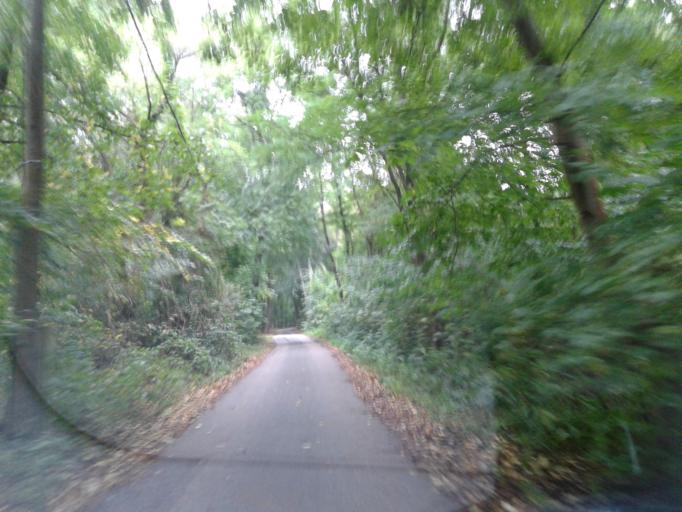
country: HU
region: Bacs-Kiskun
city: Harta
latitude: 46.6850
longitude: 19.0026
